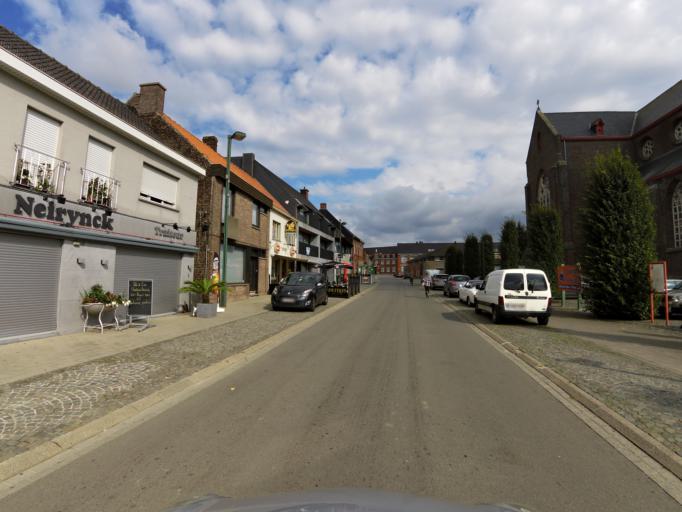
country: BE
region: Flanders
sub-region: Provincie West-Vlaanderen
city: Pittem
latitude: 51.0153
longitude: 3.2593
